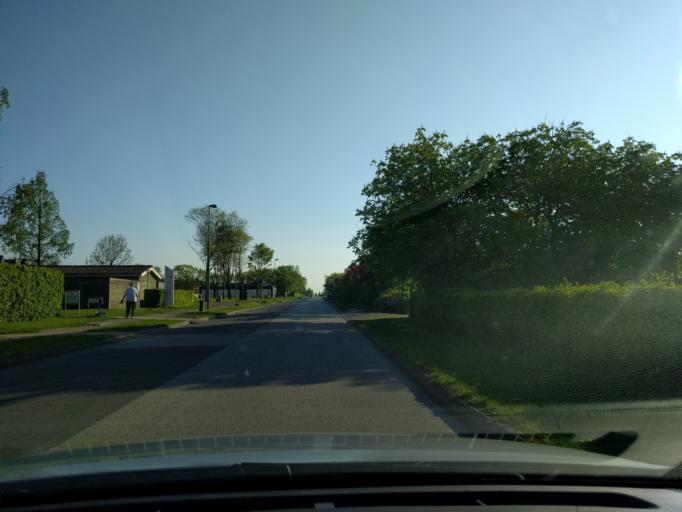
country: DK
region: Zealand
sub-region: Guldborgsund Kommune
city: Nykobing Falster
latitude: 54.7775
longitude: 11.8785
